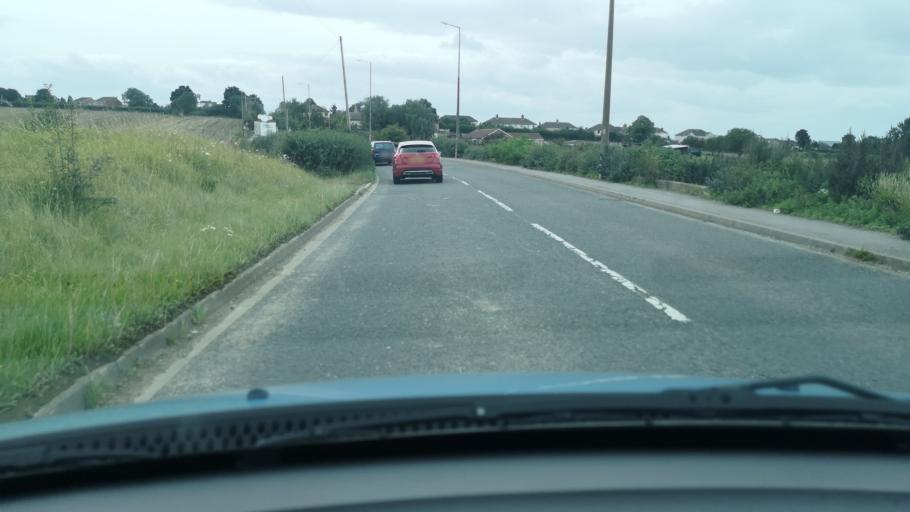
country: GB
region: England
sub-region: Barnsley
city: Grimethorpe
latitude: 53.5993
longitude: -1.3804
